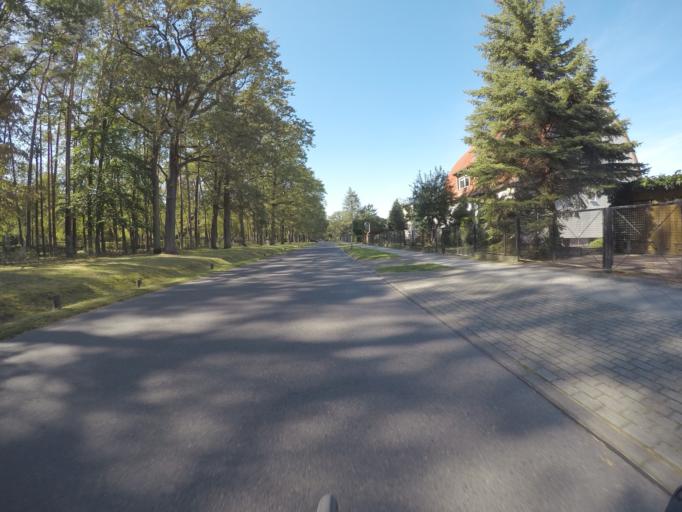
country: DE
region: Brandenburg
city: Hennigsdorf
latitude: 52.6388
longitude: 13.1897
